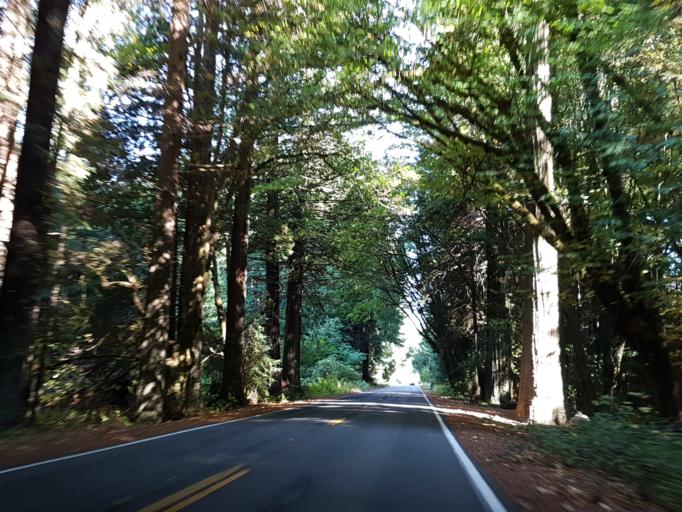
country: US
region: California
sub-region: Humboldt County
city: Rio Dell
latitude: 40.4461
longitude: -124.0034
